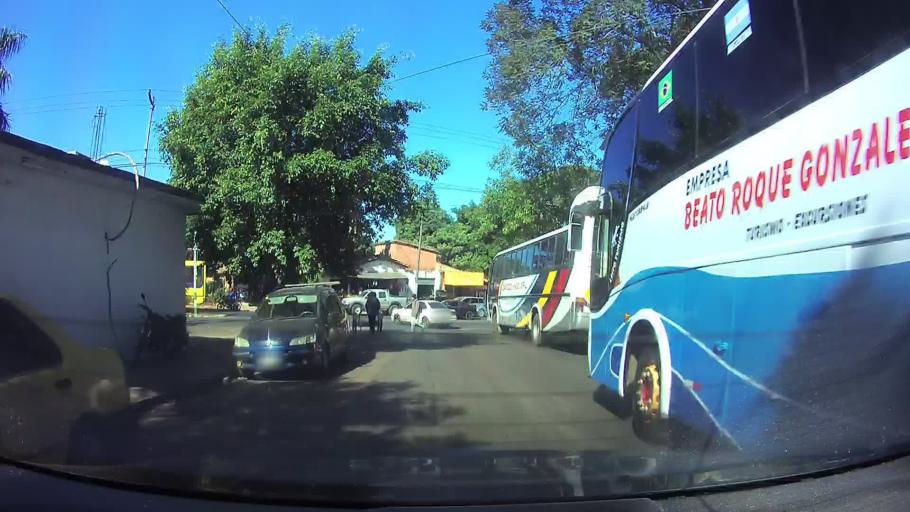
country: PY
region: Central
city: Villa Elisa
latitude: -25.3570
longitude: -57.5712
